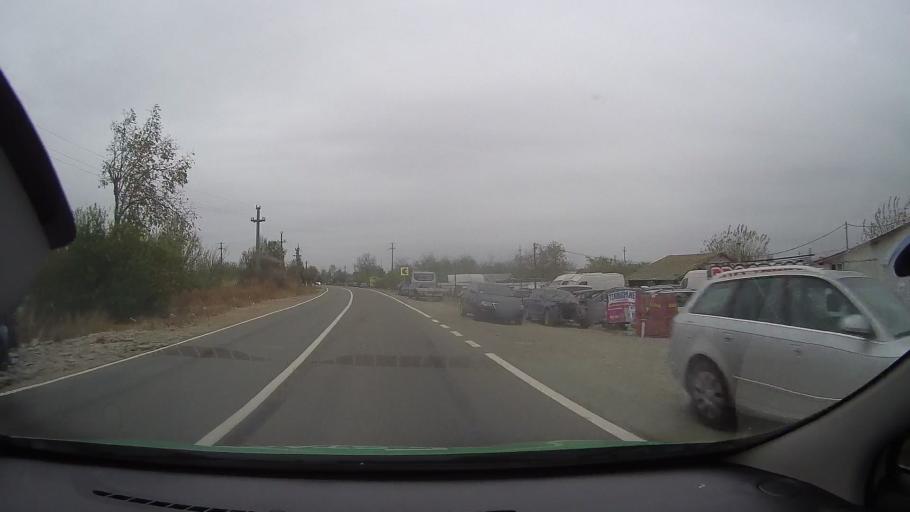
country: RO
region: Ialomita
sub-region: Comuna Slobozia
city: Slobozia
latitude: 44.6079
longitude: 27.3852
